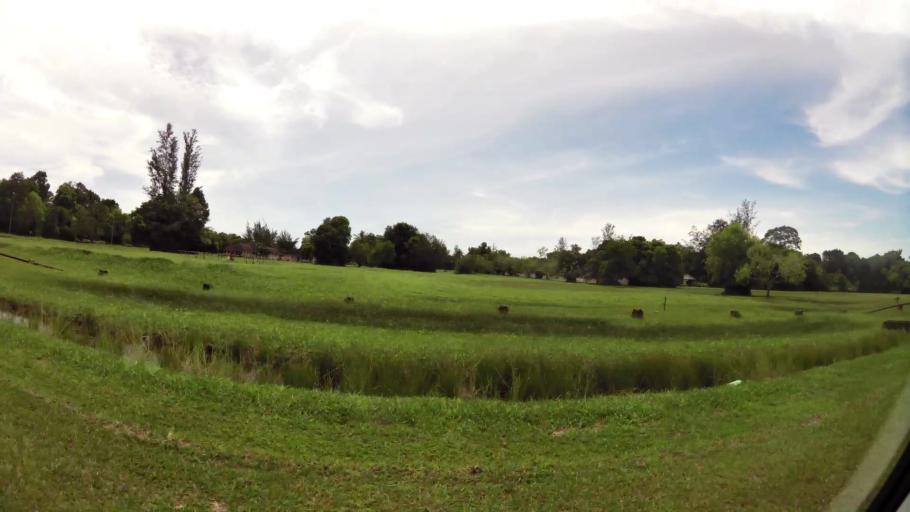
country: BN
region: Belait
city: Seria
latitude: 4.6012
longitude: 114.2899
